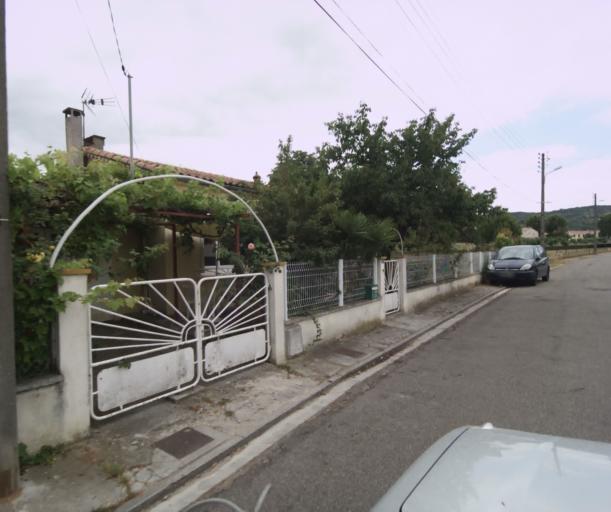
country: FR
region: Languedoc-Roussillon
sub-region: Departement de l'Aude
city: Limoux
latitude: 43.0656
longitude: 2.2187
